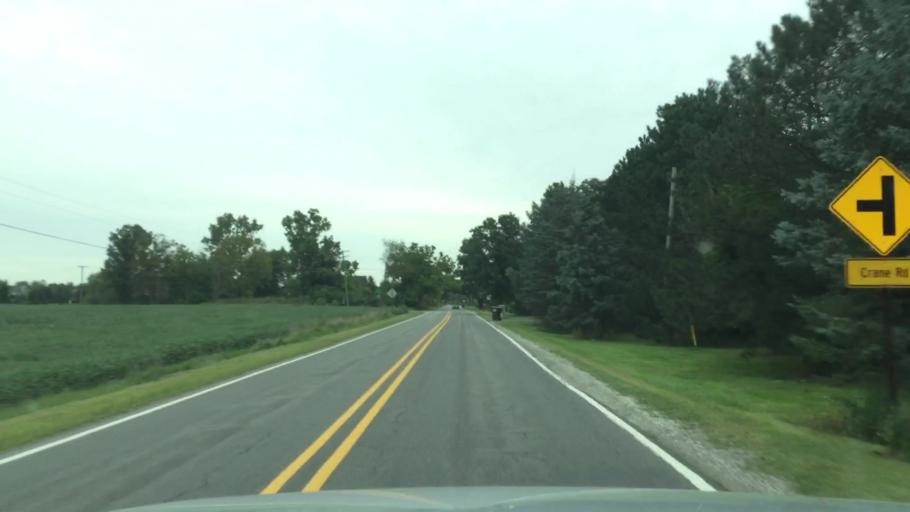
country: US
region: Michigan
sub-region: Washtenaw County
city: Milan
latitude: 42.1379
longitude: -83.6696
